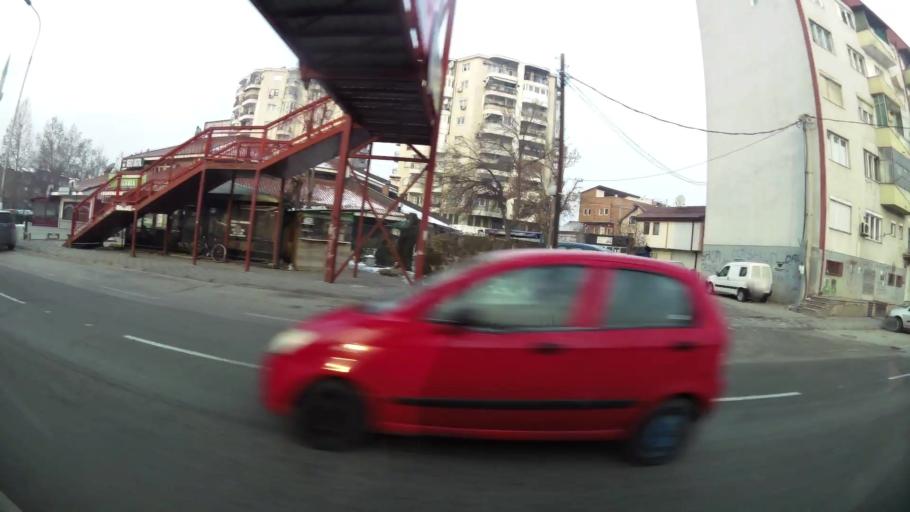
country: MK
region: Cair
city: Cair
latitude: 42.0088
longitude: 21.4435
